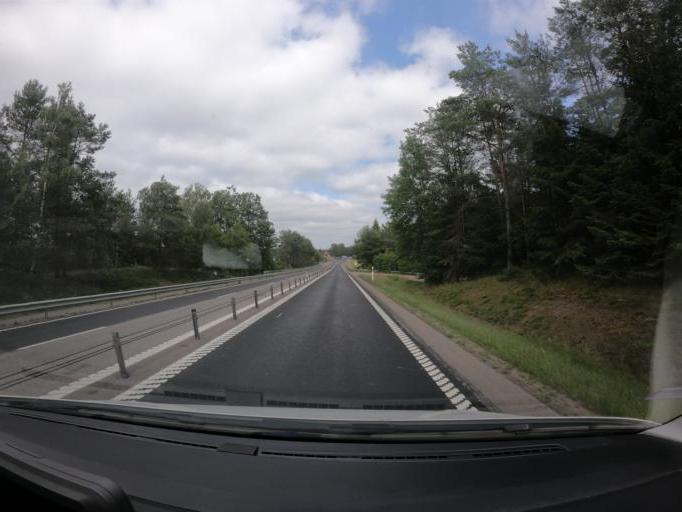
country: SE
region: Skane
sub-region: Hassleholms Kommun
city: Sosdala
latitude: 56.1604
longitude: 13.5707
